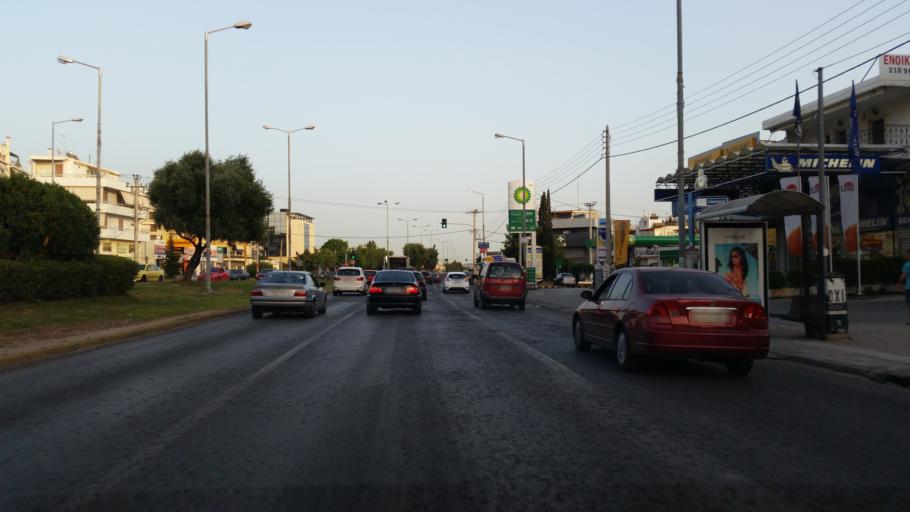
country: GR
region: Attica
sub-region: Nomarchia Athinas
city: Elliniko
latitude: 37.8873
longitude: 23.7501
